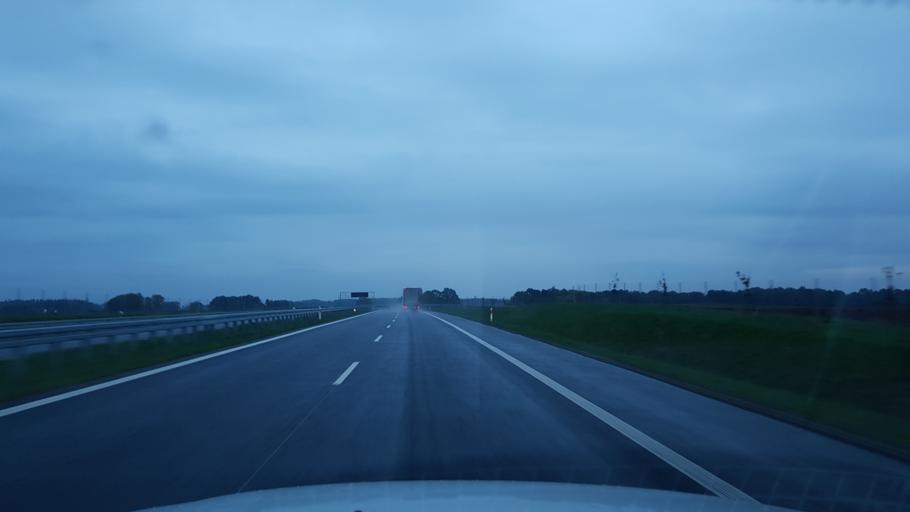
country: PL
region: West Pomeranian Voivodeship
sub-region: Powiat gryficki
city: Brojce
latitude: 53.8882
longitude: 15.3812
